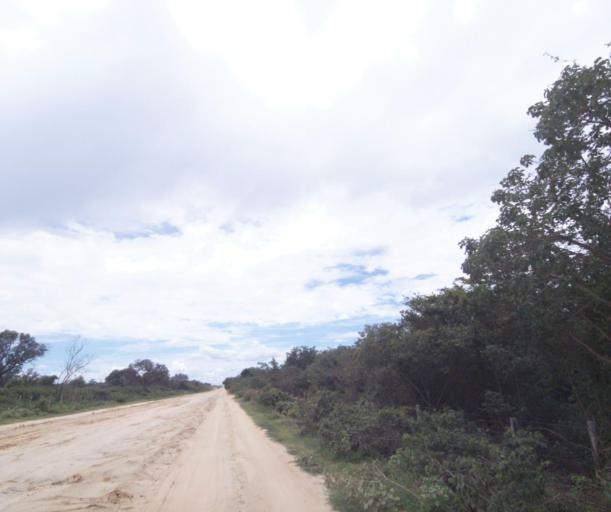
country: BR
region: Bahia
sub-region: Carinhanha
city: Carinhanha
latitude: -14.2728
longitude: -43.8047
